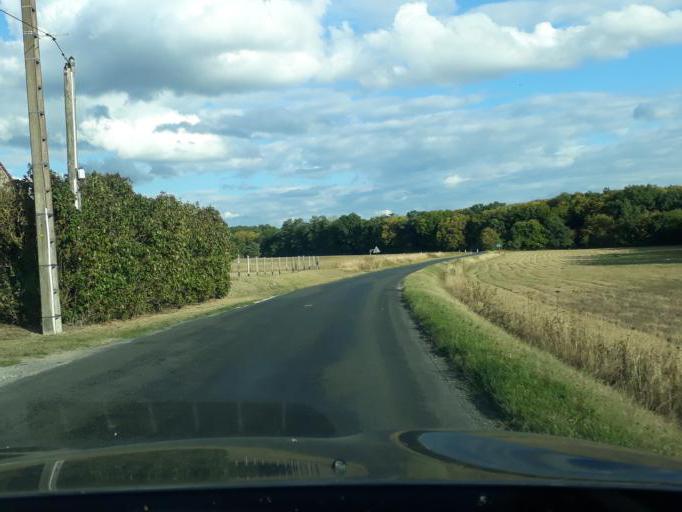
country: FR
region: Centre
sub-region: Departement du Loiret
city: Trainou
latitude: 47.9765
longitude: 2.1305
